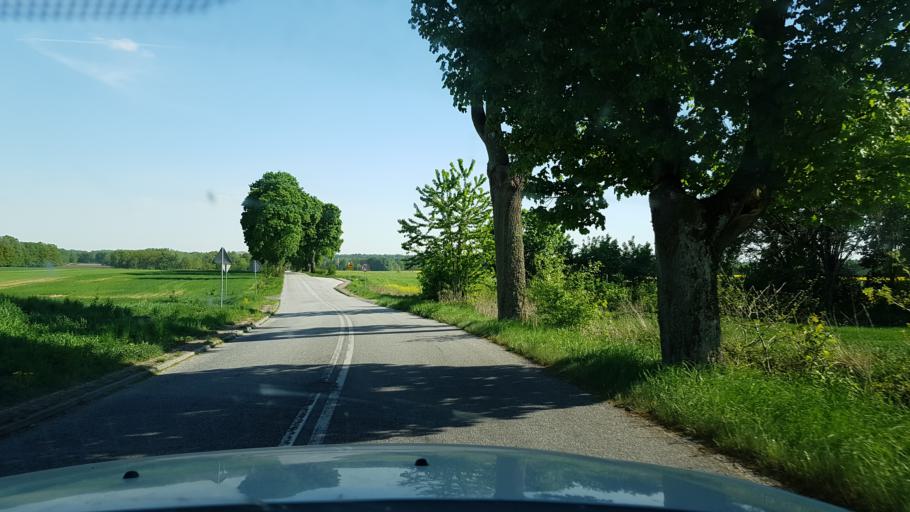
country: PL
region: West Pomeranian Voivodeship
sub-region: Powiat lobeski
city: Resko
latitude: 53.8300
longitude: 15.3885
